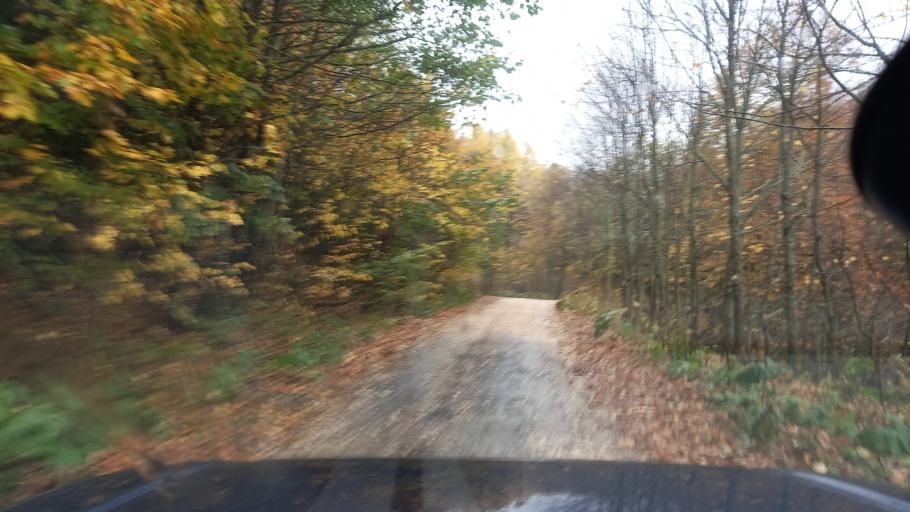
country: RU
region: Krasnodarskiy
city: Neftegorsk
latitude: 44.0151
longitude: 39.8446
